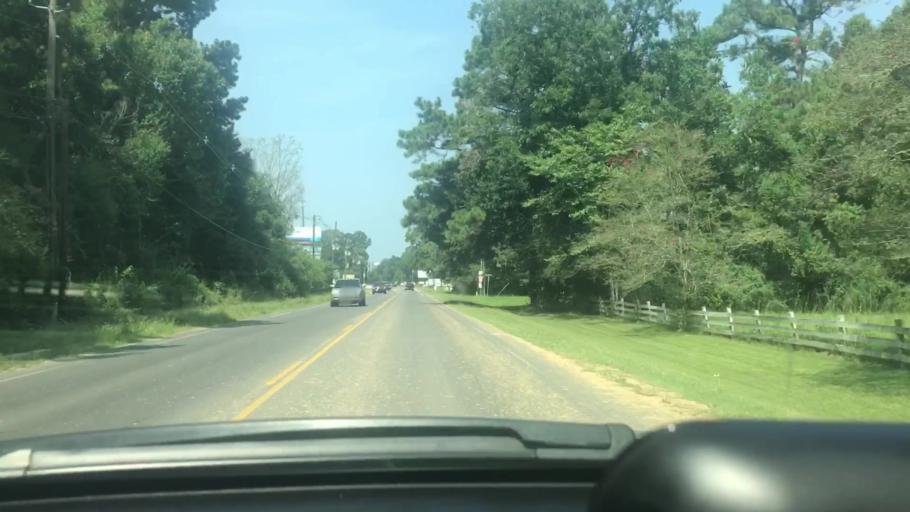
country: US
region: Louisiana
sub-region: Livingston Parish
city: Denham Springs
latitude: 30.4837
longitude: -90.9329
